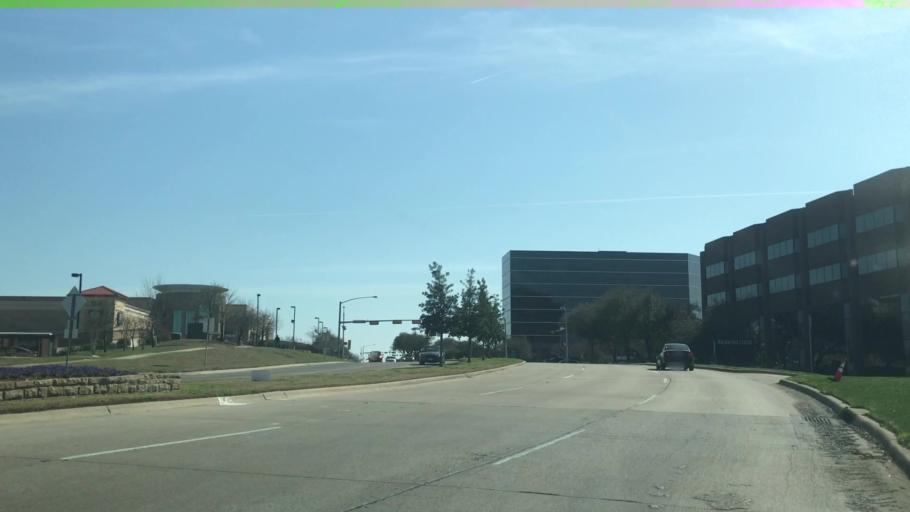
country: US
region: Texas
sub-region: Dallas County
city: Irving
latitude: 32.8887
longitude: -96.9640
